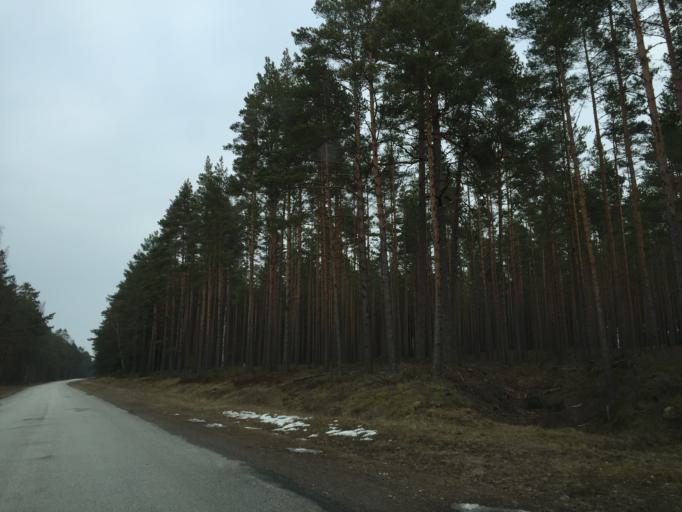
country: LV
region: Salacgrivas
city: Ainazi
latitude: 57.9742
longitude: 24.4119
